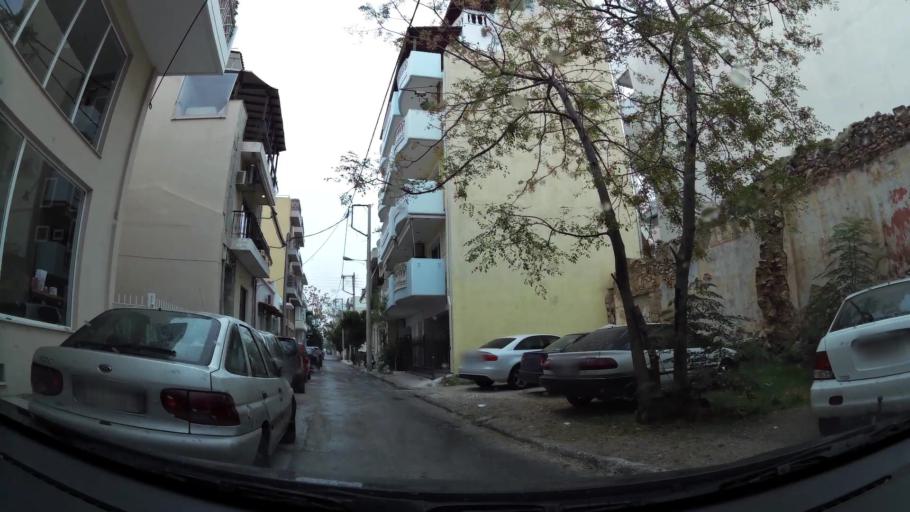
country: GR
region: Attica
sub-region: Nomos Piraios
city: Nikaia
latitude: 37.9572
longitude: 23.6500
